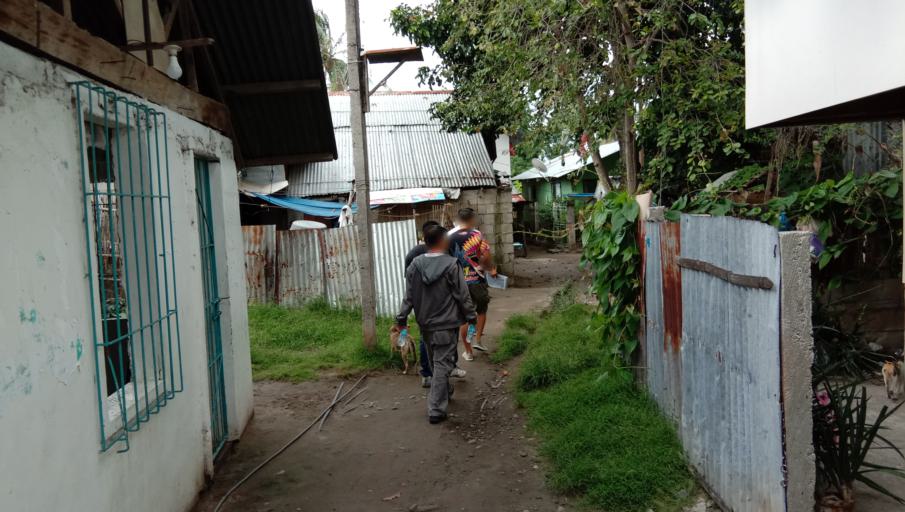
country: PH
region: Central Visayas
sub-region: Province of Negros Oriental
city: Dumaguete
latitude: 9.3028
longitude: 123.3018
